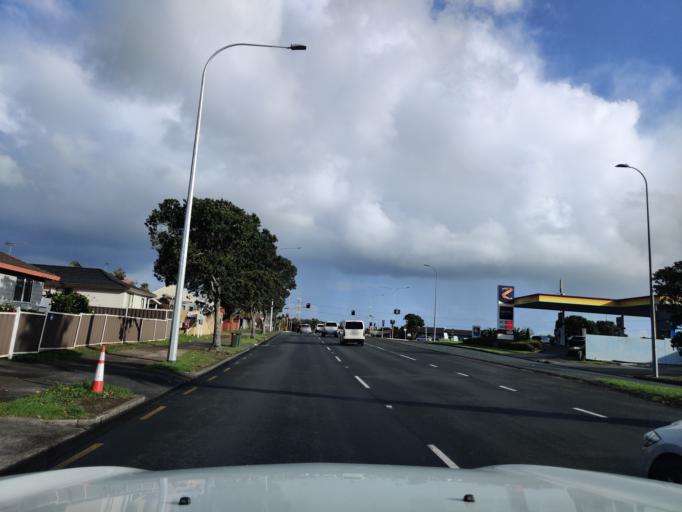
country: NZ
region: Auckland
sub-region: Auckland
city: Manukau City
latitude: -36.9770
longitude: 174.8982
